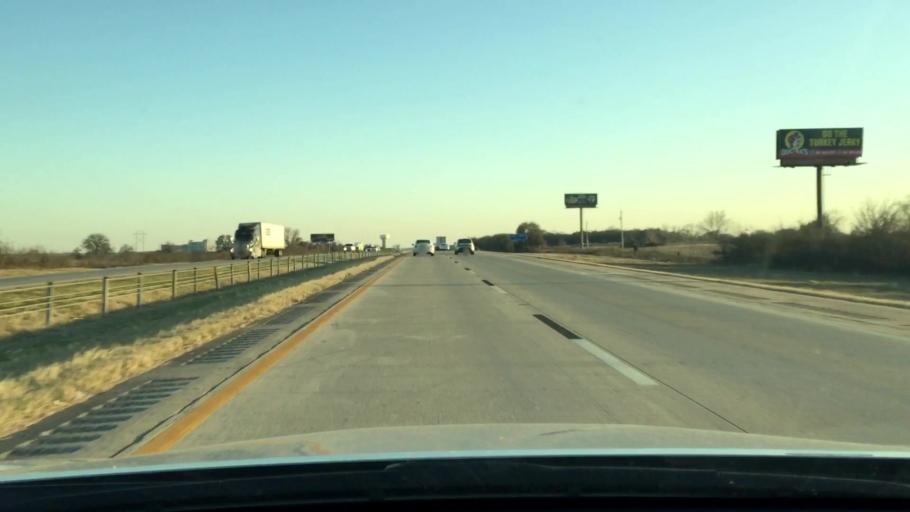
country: US
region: Oklahoma
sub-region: Love County
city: Marietta
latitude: 33.7850
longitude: -97.1350
